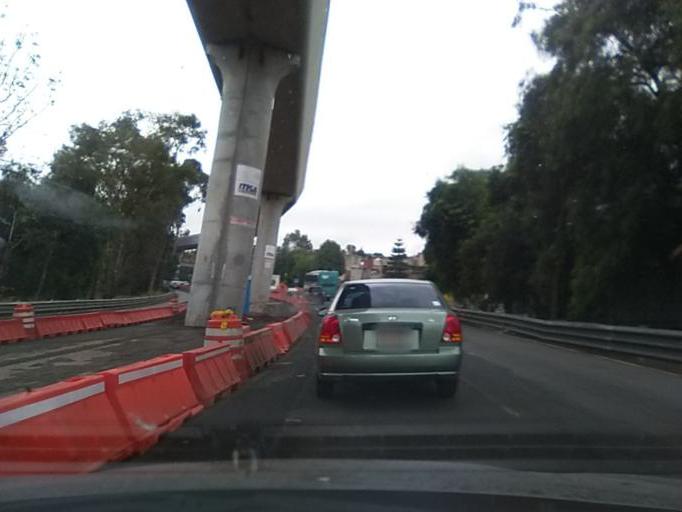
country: MX
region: Mexico City
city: Tlalpan
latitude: 19.2499
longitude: -99.1559
